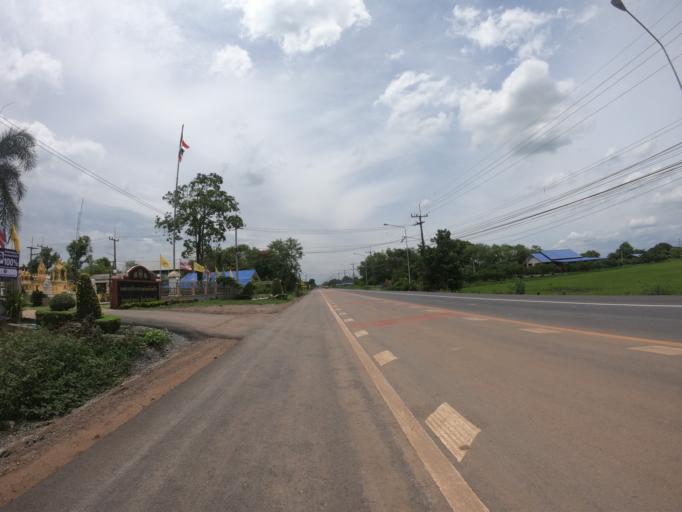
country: TH
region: Pathum Thani
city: Nong Suea
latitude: 14.0357
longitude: 100.8699
